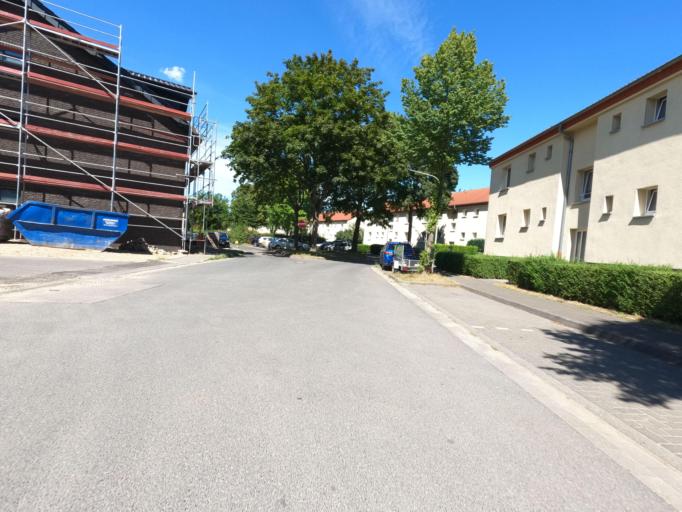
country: DE
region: North Rhine-Westphalia
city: Baesweiler
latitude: 50.9127
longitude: 6.1798
